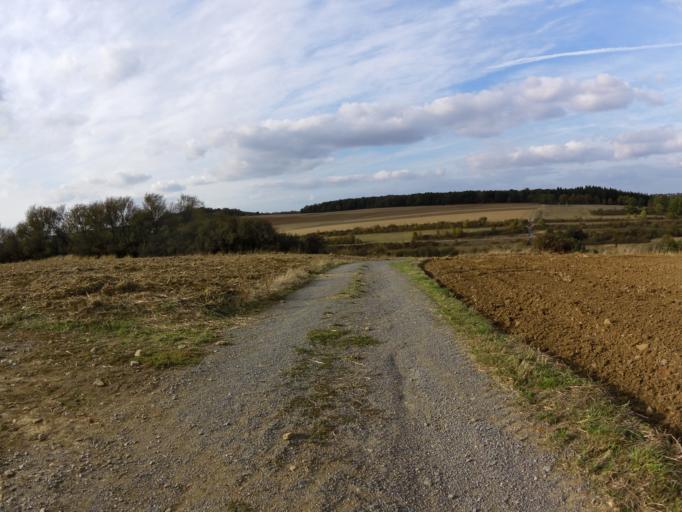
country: DE
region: Bavaria
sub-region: Regierungsbezirk Unterfranken
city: Reichenberg
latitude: 49.7284
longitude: 9.9442
